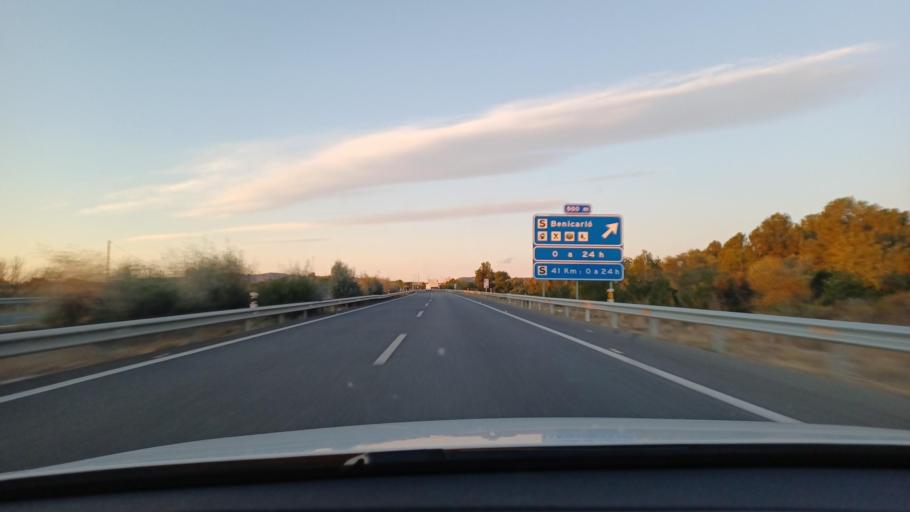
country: ES
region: Valencia
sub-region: Provincia de Castello
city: Benicarlo
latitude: 40.4666
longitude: 0.4138
